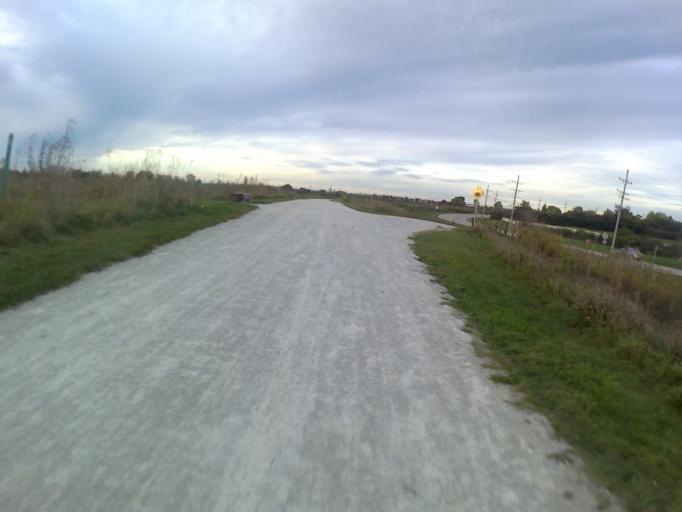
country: US
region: Illinois
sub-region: DuPage County
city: Lisle
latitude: 41.8232
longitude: -88.0993
